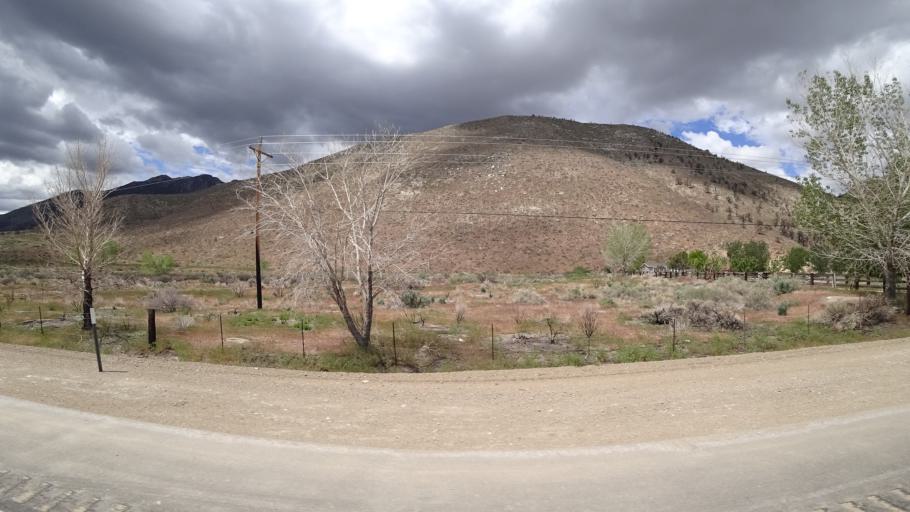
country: US
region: Nevada
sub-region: Lyon County
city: Smith Valley
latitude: 38.6381
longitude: -119.5258
